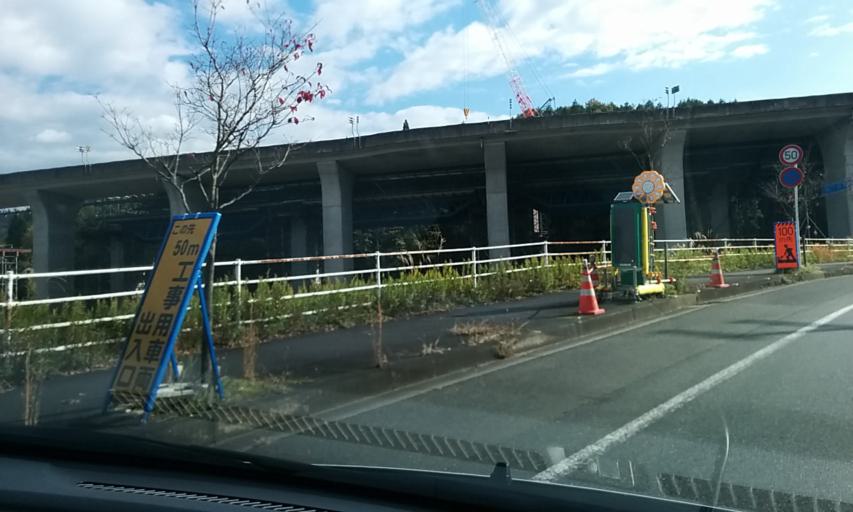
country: JP
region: Kyoto
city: Fukuchiyama
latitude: 35.2947
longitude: 135.1783
